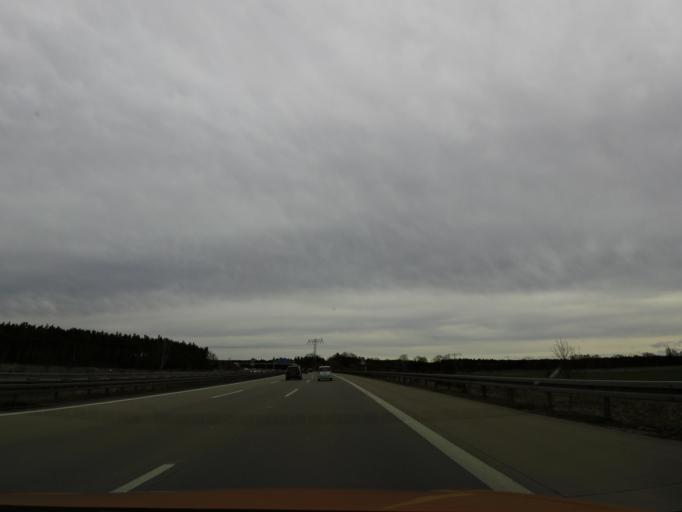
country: DE
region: Berlin
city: Wannsee
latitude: 52.3378
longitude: 13.1362
